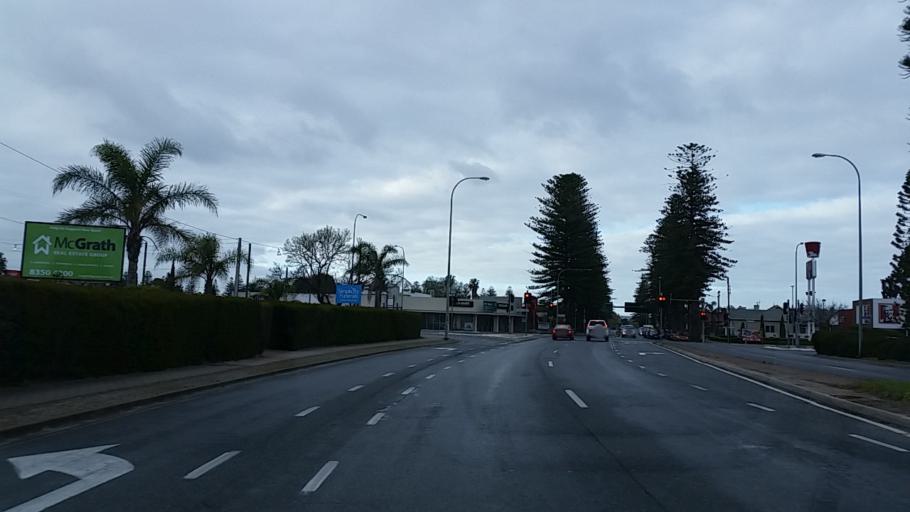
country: AU
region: South Australia
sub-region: Adelaide
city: Glenelg
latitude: -34.9755
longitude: 138.5198
